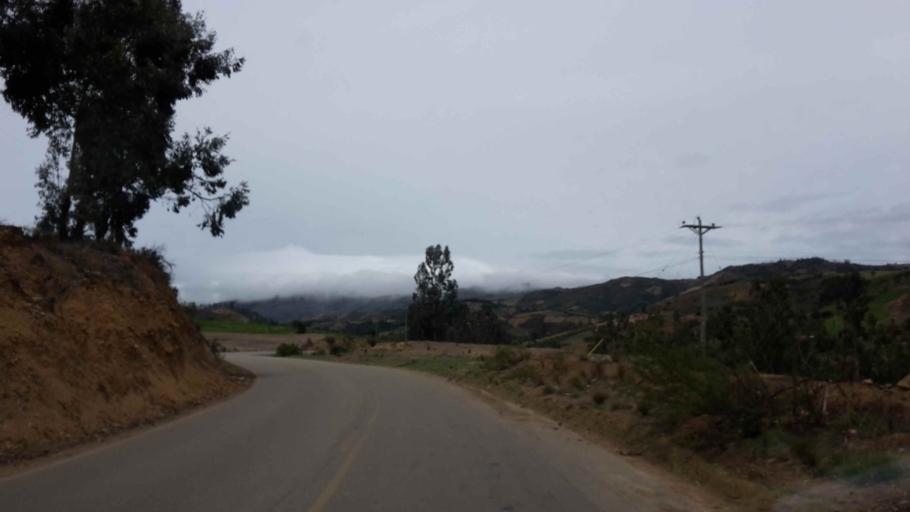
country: BO
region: Cochabamba
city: Totora
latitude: -17.6991
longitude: -65.2149
